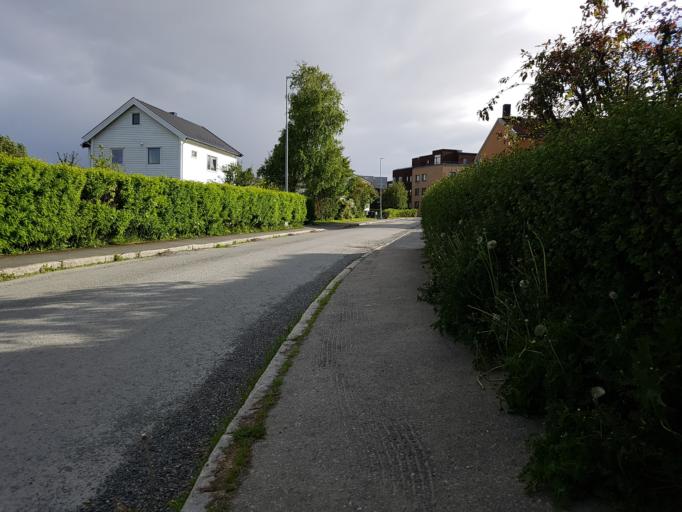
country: NO
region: Sor-Trondelag
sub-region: Trondheim
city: Trondheim
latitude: 63.4311
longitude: 10.4627
